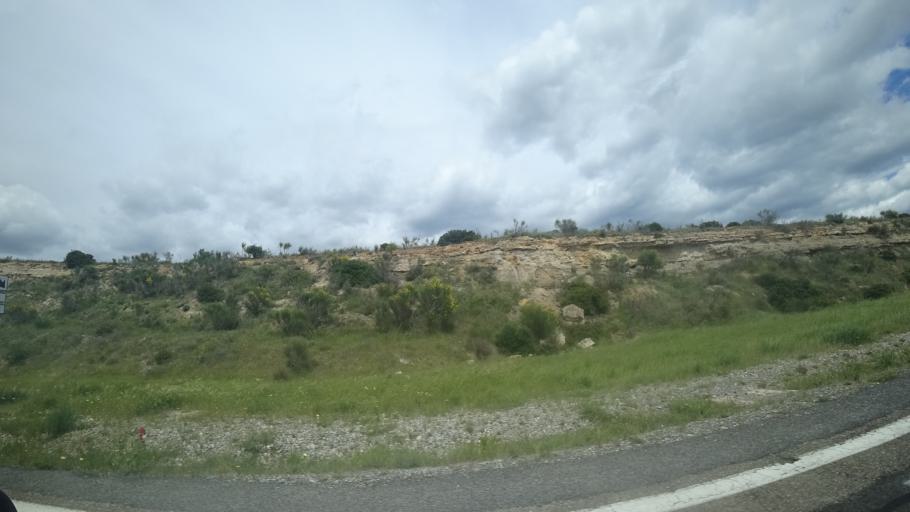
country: FR
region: Languedoc-Roussillon
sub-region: Departement de l'Aude
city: Leucate
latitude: 42.9290
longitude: 3.0173
